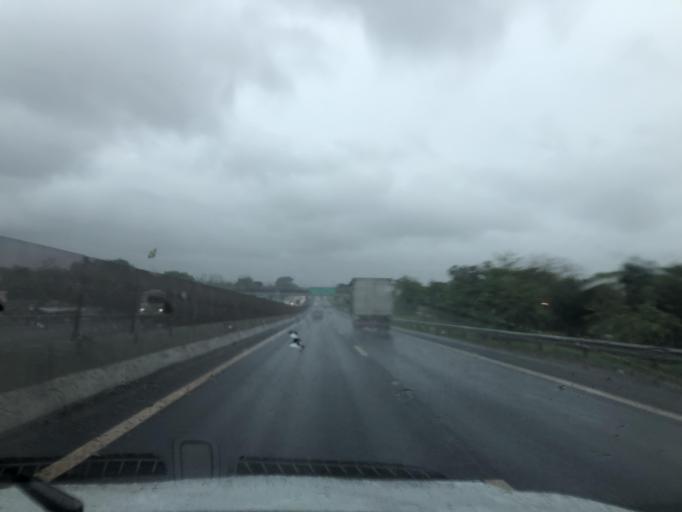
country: BR
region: Sao Paulo
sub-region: Ribeirao Preto
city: Ribeirao Preto
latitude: -21.1904
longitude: -47.7575
